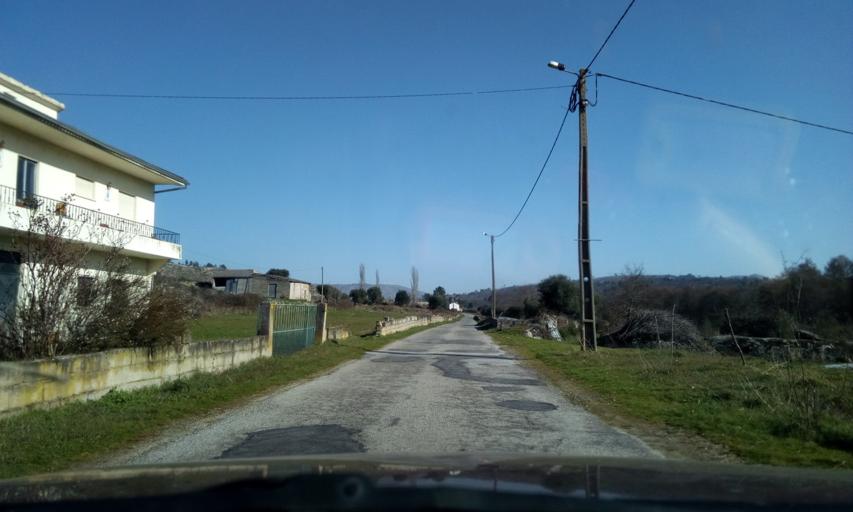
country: PT
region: Guarda
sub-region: Celorico da Beira
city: Celorico da Beira
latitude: 40.6640
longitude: -7.4603
